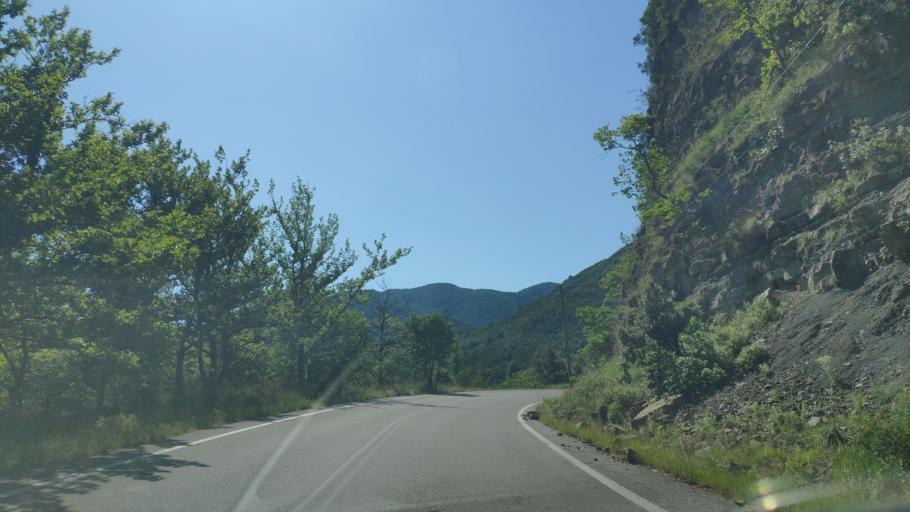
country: GR
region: West Greece
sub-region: Nomos Aitolias kai Akarnanias
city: Sardinia
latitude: 38.9241
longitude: 21.3571
